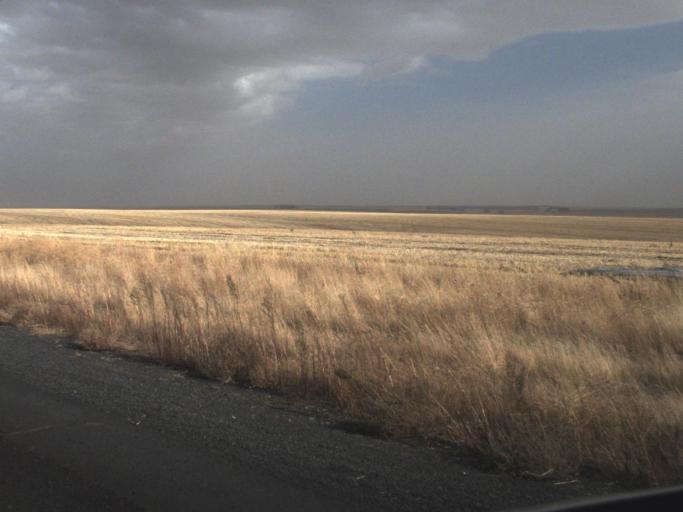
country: US
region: Washington
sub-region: Lincoln County
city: Davenport
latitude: 47.4371
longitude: -118.3313
